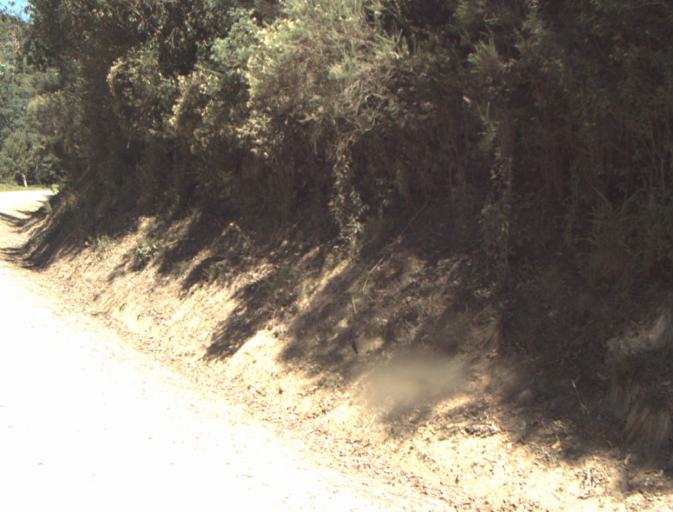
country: AU
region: Tasmania
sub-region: Dorset
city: Scottsdale
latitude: -41.3194
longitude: 147.4143
